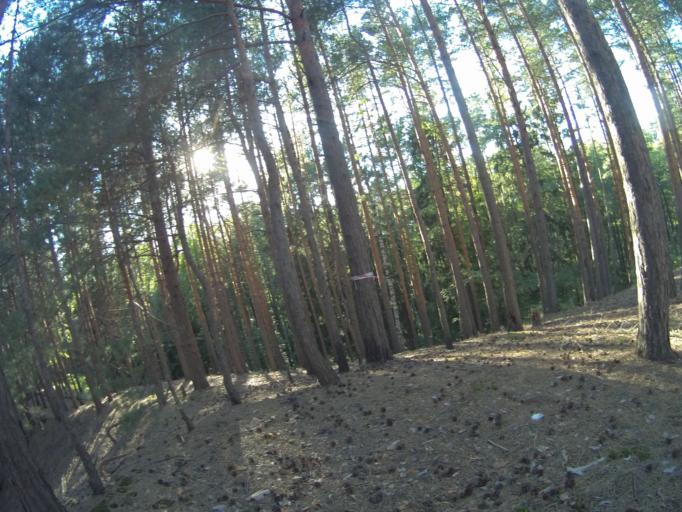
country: RU
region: Vladimir
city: Kommunar
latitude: 56.0486
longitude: 40.4353
